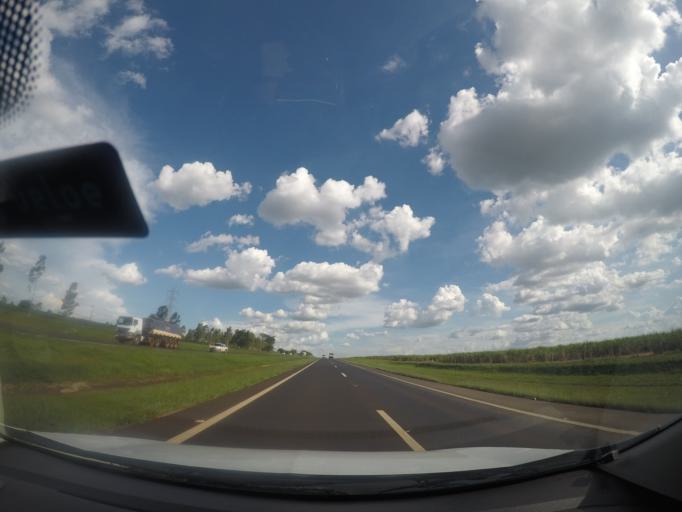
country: BR
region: Sao Paulo
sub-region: Bebedouro
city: Bebedouro
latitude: -20.8564
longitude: -48.4774
